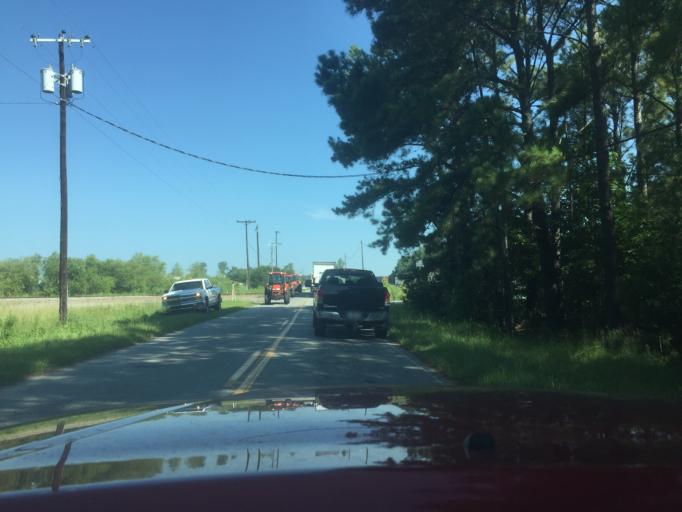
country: US
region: Georgia
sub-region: Chatham County
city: Garden City
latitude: 32.0758
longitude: -81.1438
